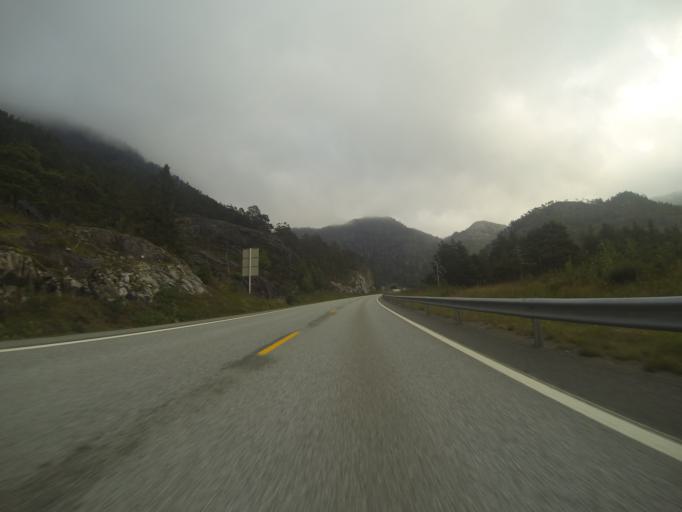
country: NO
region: Hordaland
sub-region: Odda
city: Odda
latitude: 59.8806
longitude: 6.4330
